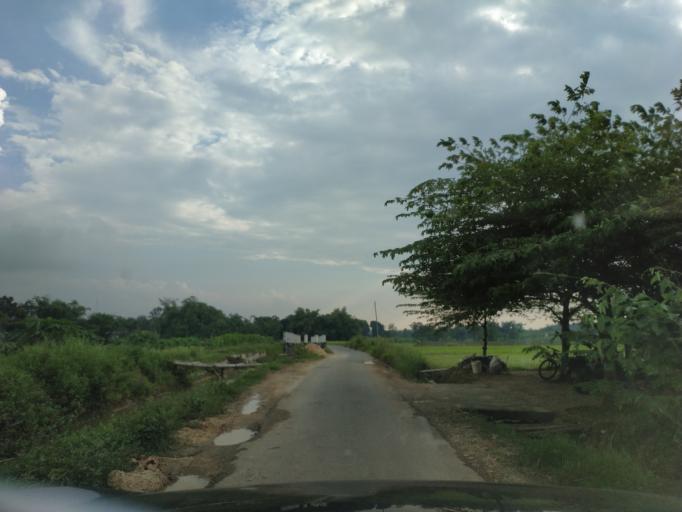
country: ID
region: Central Java
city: Tempuran
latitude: -6.9093
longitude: 111.4612
